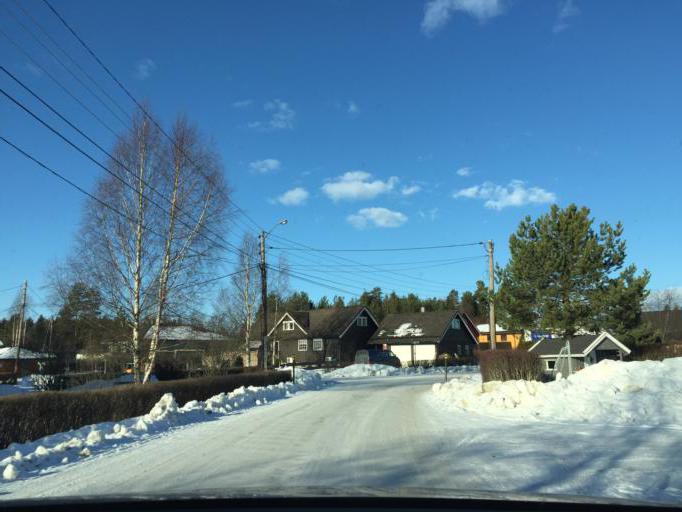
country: NO
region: Akershus
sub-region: Nes
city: Fjellfoten
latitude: 60.0870
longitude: 11.4711
